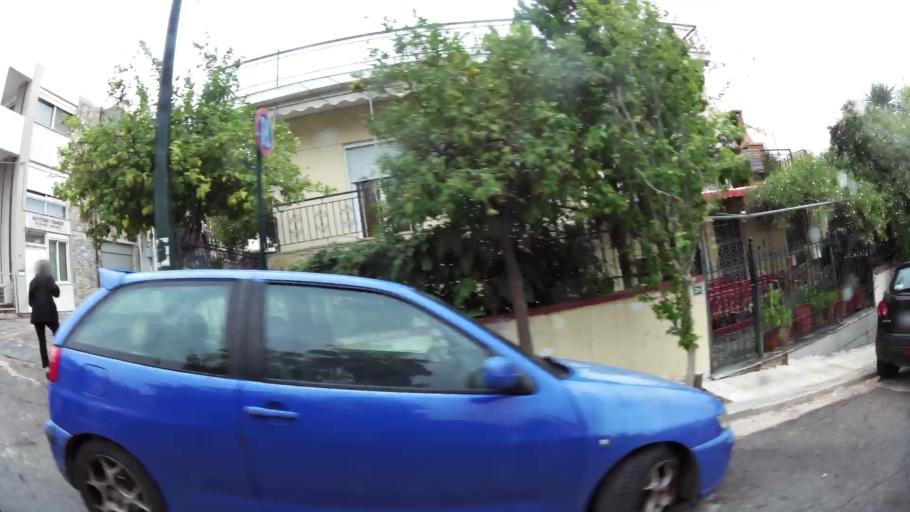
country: GR
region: Attica
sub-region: Nomarchia Athinas
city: Agia Varvara
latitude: 37.9924
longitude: 23.6528
